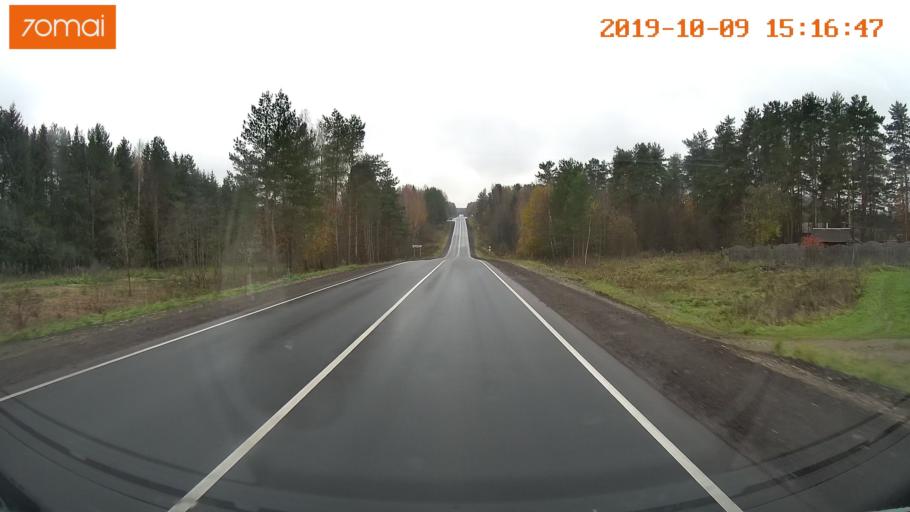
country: RU
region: Kostroma
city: Susanino
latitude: 58.1068
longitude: 41.5850
